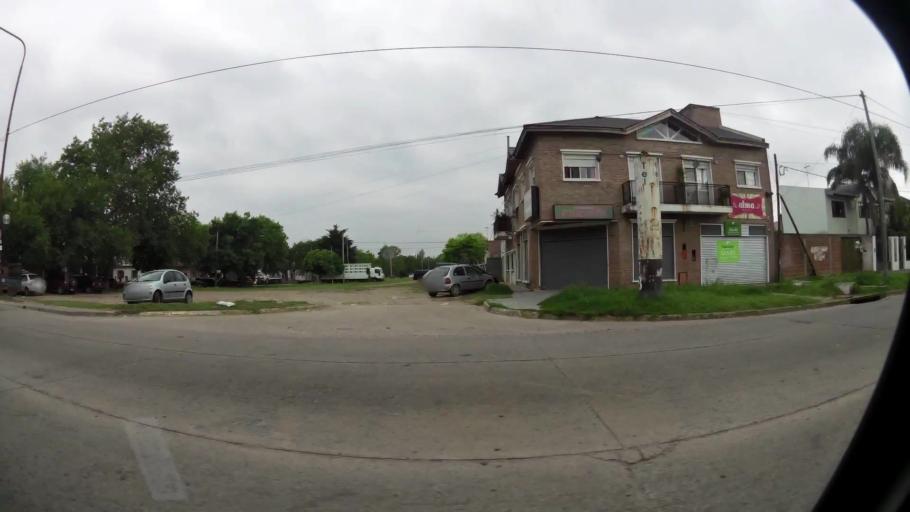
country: AR
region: Buenos Aires
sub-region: Partido de La Plata
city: La Plata
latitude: -34.8943
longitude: -57.9869
